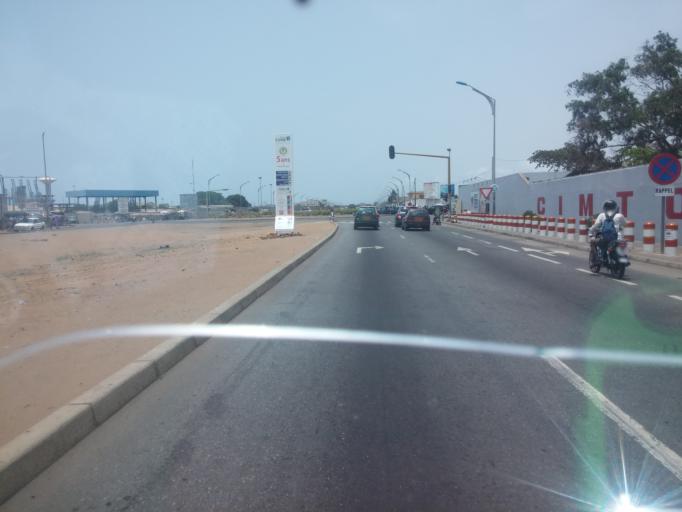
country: TG
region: Maritime
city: Lome
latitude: 6.1516
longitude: 1.2875
